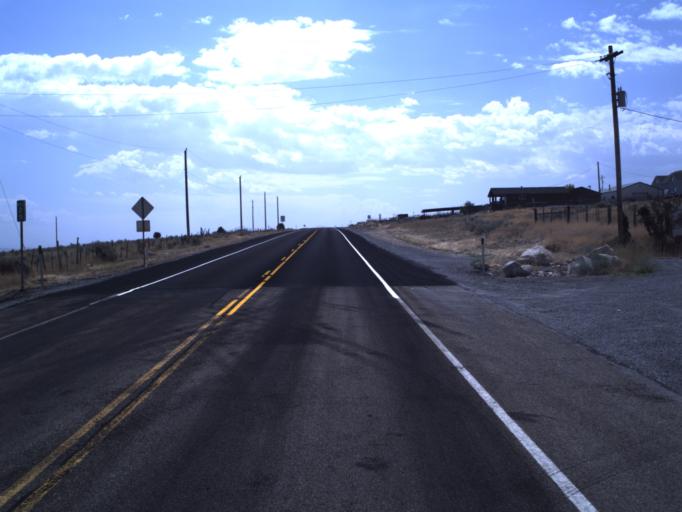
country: US
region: Utah
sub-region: Utah County
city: Eagle Mountain
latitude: 40.3230
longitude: -112.1024
